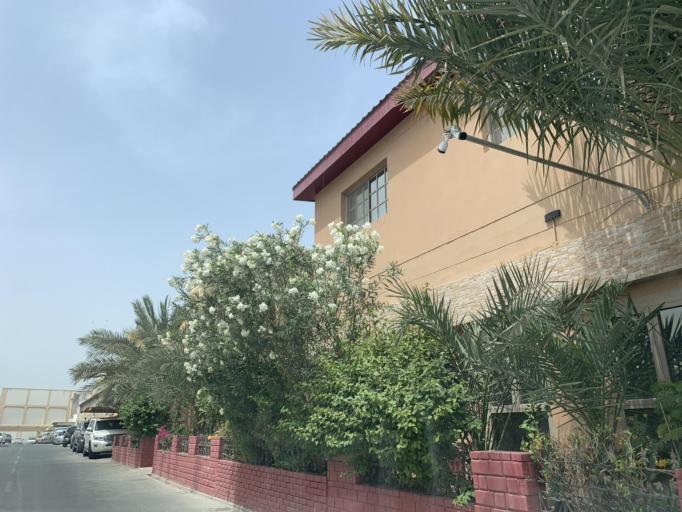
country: BH
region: Northern
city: Ar Rifa'
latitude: 26.1340
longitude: 50.5652
